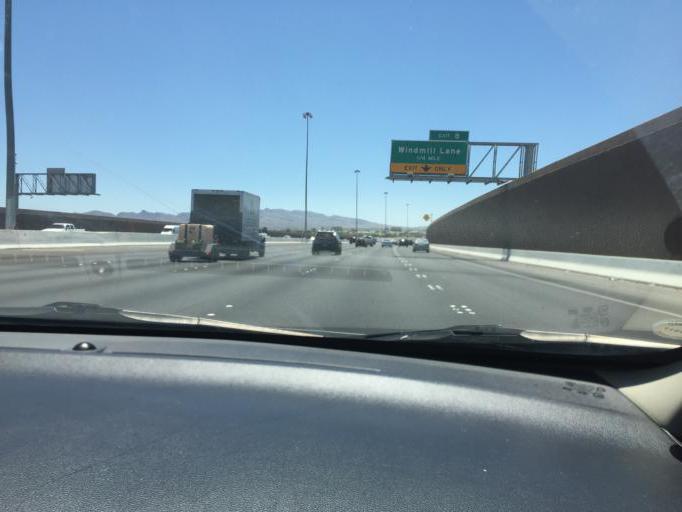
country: US
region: Nevada
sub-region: Clark County
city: Paradise
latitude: 36.0497
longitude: -115.1359
